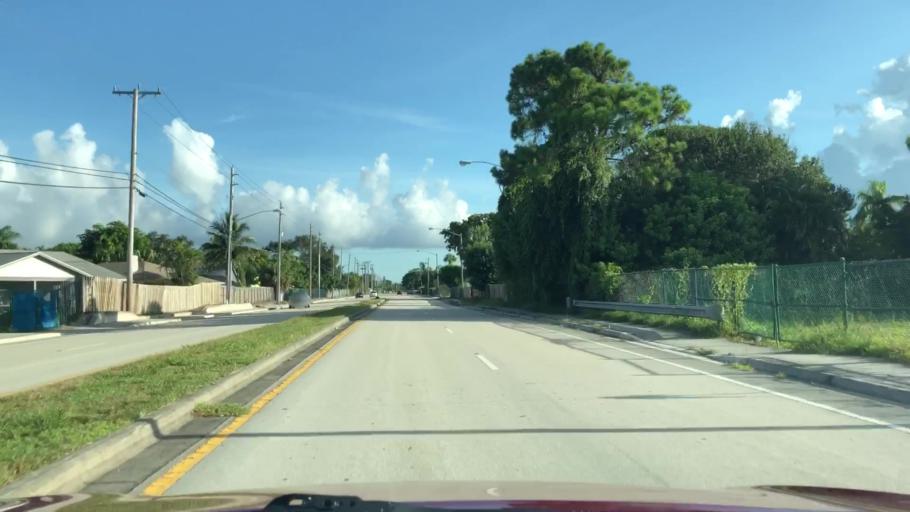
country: US
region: Florida
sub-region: Palm Beach County
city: Boynton Beach
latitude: 26.5349
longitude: -80.1066
